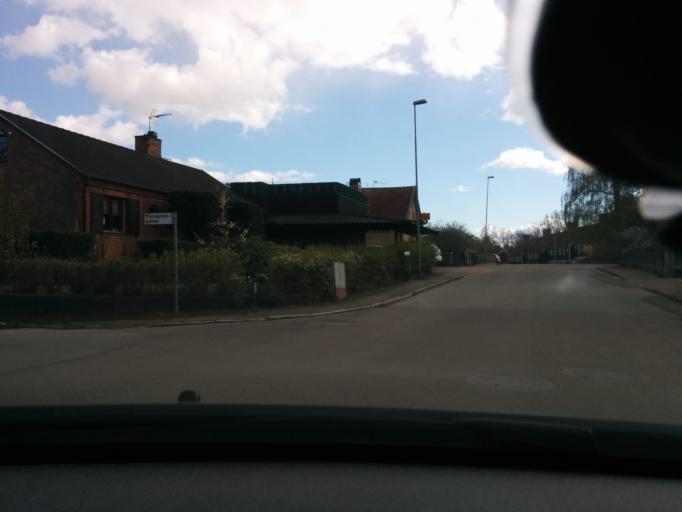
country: SE
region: Vaestmanland
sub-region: Vasteras
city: Vasteras
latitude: 59.6019
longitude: 16.5999
